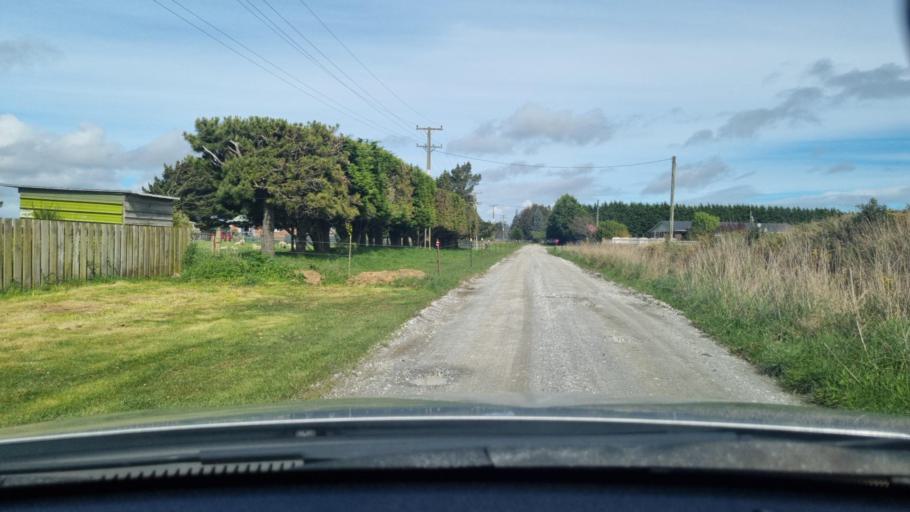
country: NZ
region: Southland
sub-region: Invercargill City
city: Invercargill
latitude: -46.4527
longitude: 168.3781
